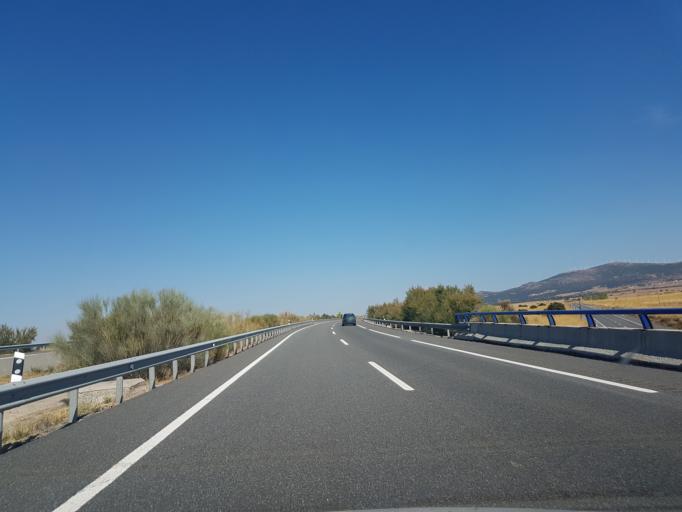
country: ES
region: Castille and Leon
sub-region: Provincia de Avila
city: Berrocalejo de Aragona
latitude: 40.6971
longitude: -4.5804
